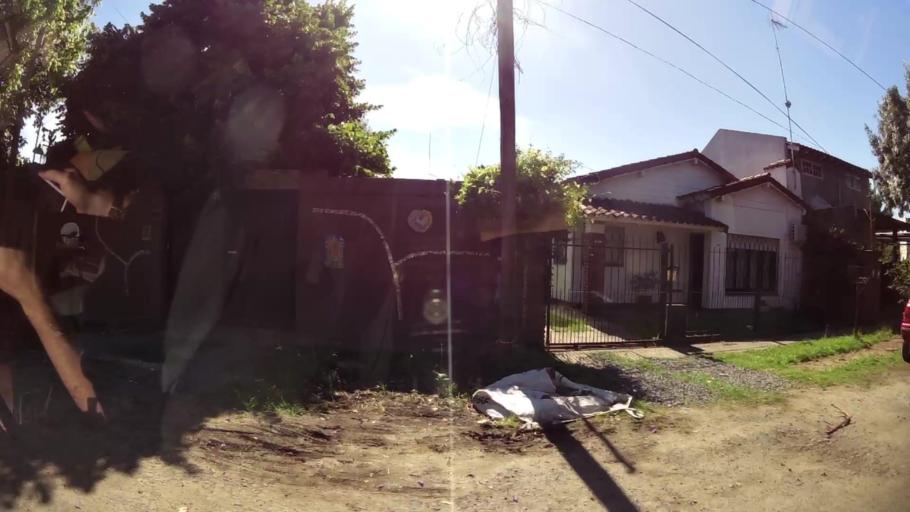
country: AR
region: Buenos Aires
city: Ituzaingo
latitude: -34.6309
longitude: -58.6566
